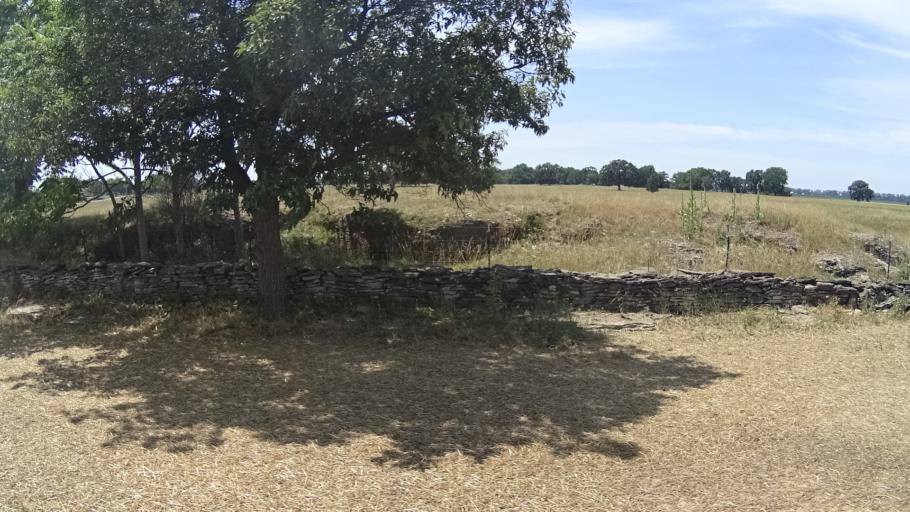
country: US
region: Ohio
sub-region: Erie County
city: Sandusky
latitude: 41.4084
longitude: -82.7715
